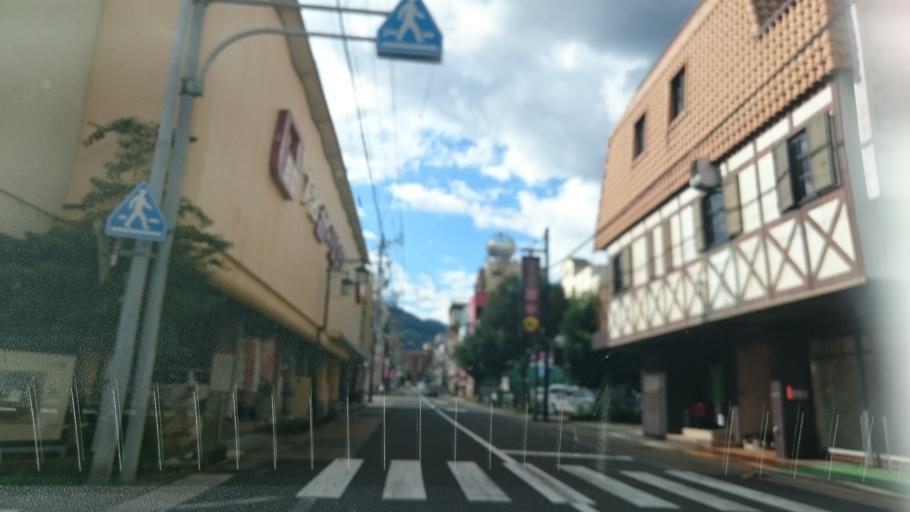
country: JP
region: Gifu
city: Gujo
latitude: 35.8041
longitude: 137.2450
